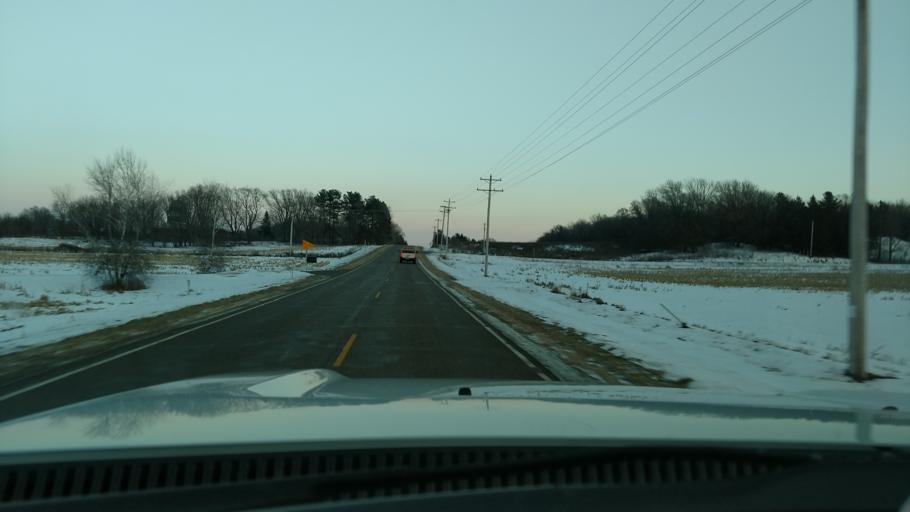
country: US
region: Wisconsin
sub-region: Saint Croix County
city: Roberts
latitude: 44.9133
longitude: -92.5196
